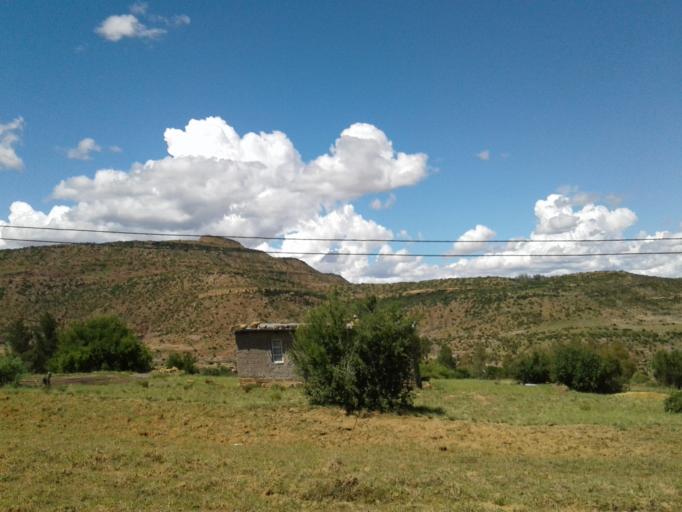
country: LS
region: Quthing
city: Quthing
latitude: -30.3651
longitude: 27.5480
